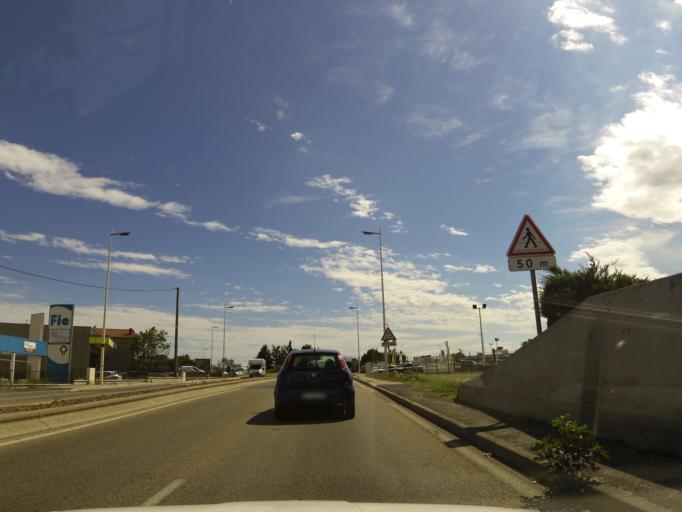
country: FR
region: Languedoc-Roussillon
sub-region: Departement du Gard
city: Ales
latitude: 44.1309
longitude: 4.1060
